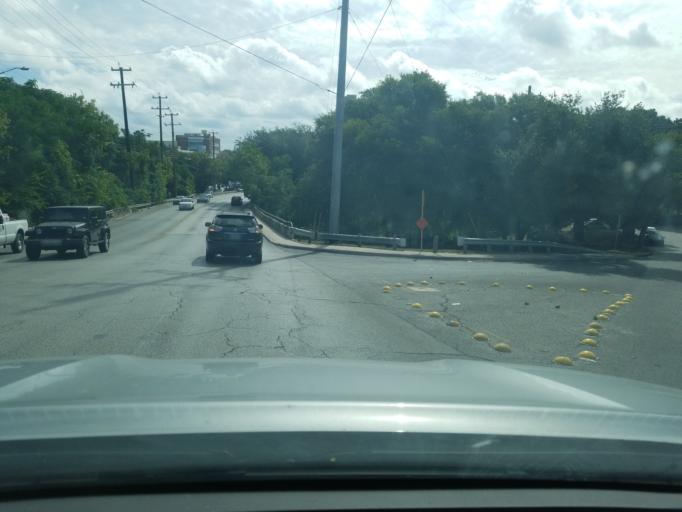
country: US
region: Texas
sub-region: Bexar County
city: Alamo Heights
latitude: 29.4656
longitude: -98.4696
